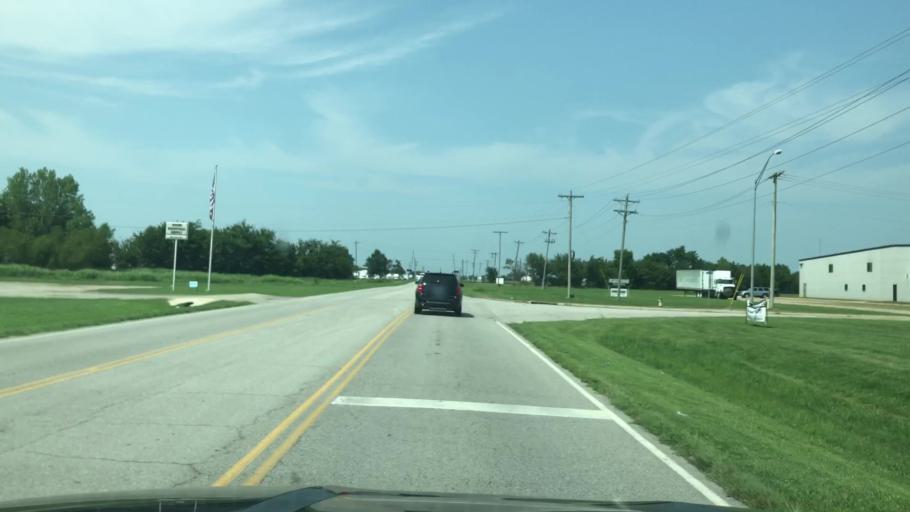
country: US
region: Oklahoma
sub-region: Ottawa County
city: Commerce
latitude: 36.9105
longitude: -94.8419
